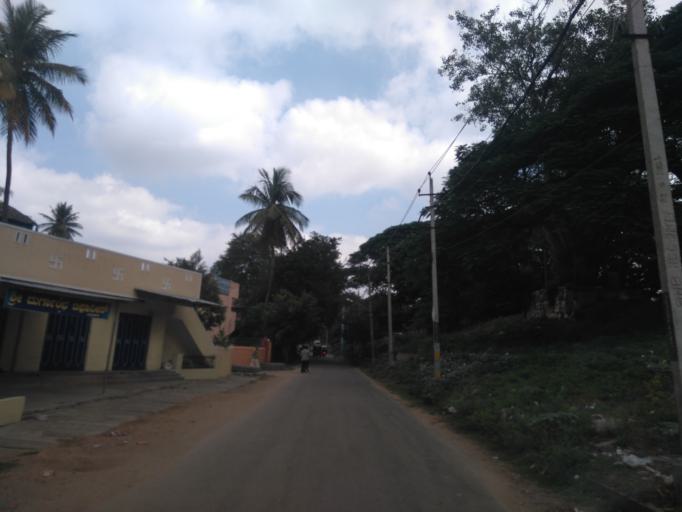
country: IN
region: Karnataka
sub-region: Mysore
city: Mysore
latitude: 12.2991
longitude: 76.6572
